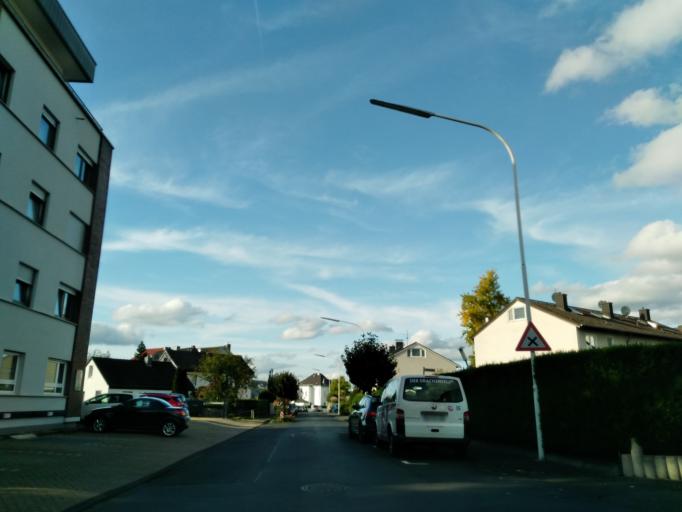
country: DE
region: Rheinland-Pfalz
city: Rheinbreitbach
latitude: 50.6204
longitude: 7.2301
